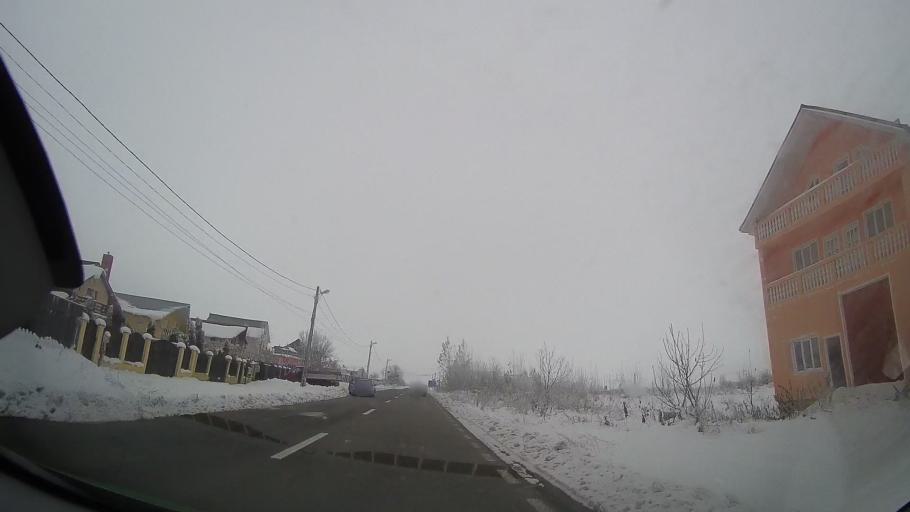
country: RO
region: Neamt
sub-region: Comuna Horia
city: Cotu Vames
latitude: 46.9367
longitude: 26.9465
